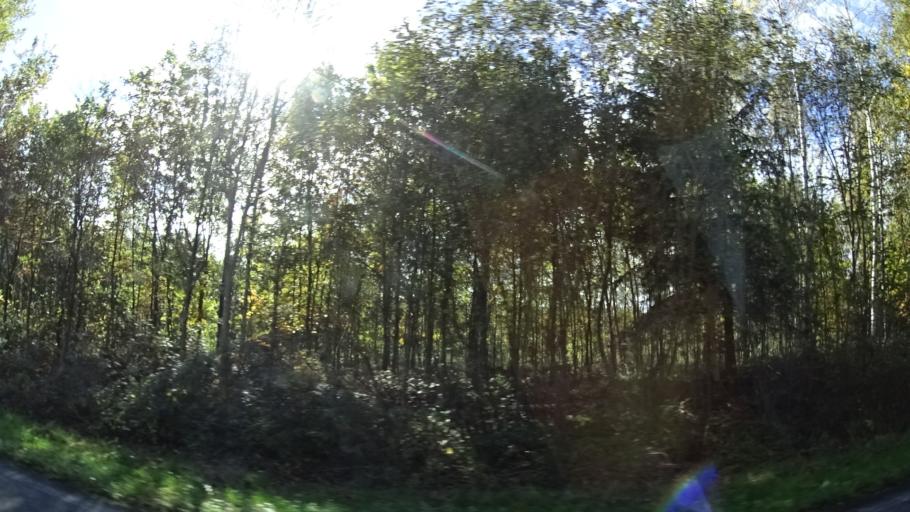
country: DE
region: Baden-Wuerttemberg
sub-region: Karlsruhe Region
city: Tiefenbronn
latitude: 48.8410
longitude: 8.8042
